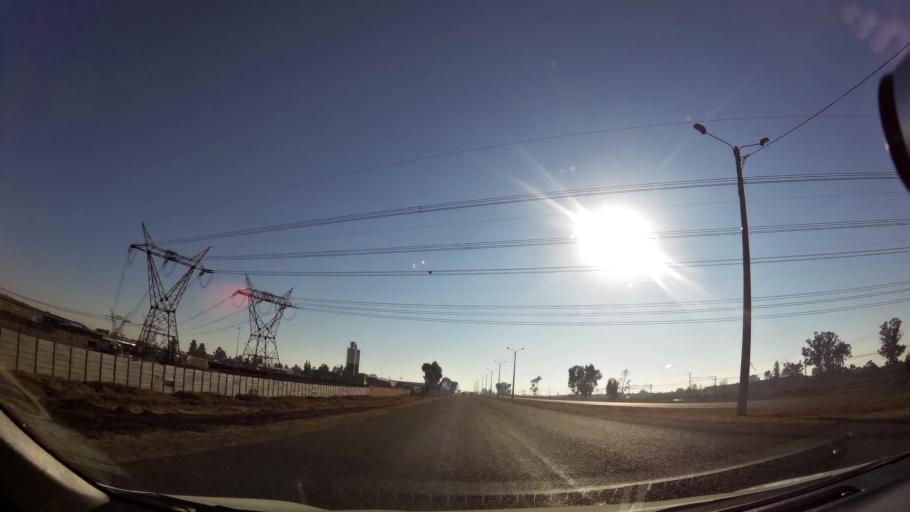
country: ZA
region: Gauteng
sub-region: Ekurhuleni Metropolitan Municipality
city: Germiston
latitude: -26.3579
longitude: 28.1204
